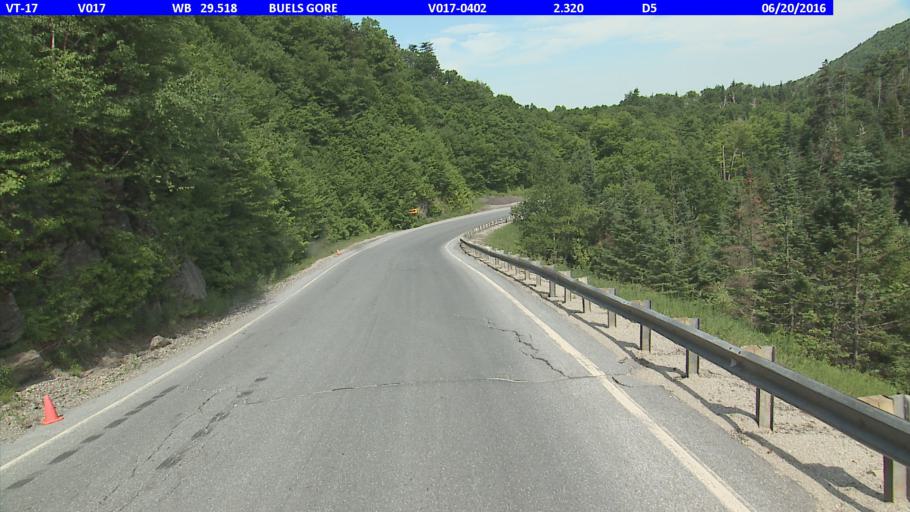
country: US
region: Vermont
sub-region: Addison County
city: Bristol
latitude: 44.2112
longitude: -72.9350
